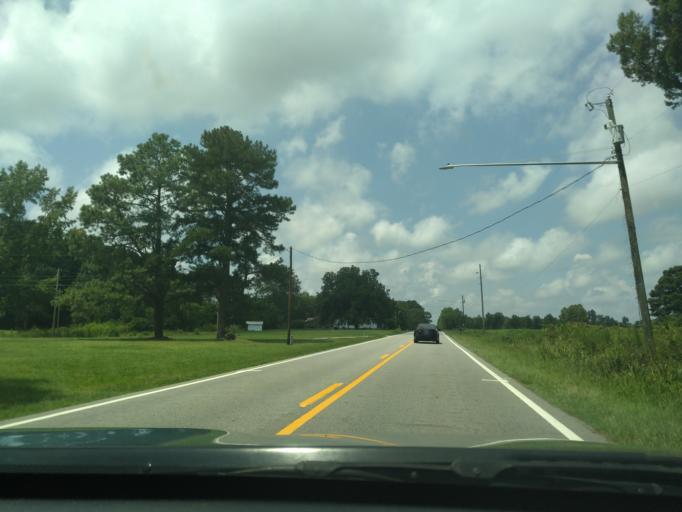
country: US
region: North Carolina
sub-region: Nash County
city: Red Oak
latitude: 36.0056
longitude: -77.8467
